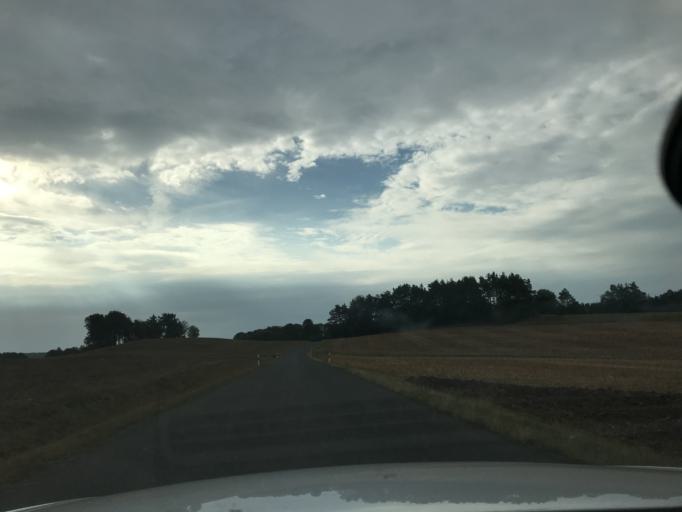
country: DE
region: Bavaria
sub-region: Upper Franconia
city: Pegnitz
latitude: 49.7382
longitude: 11.5743
